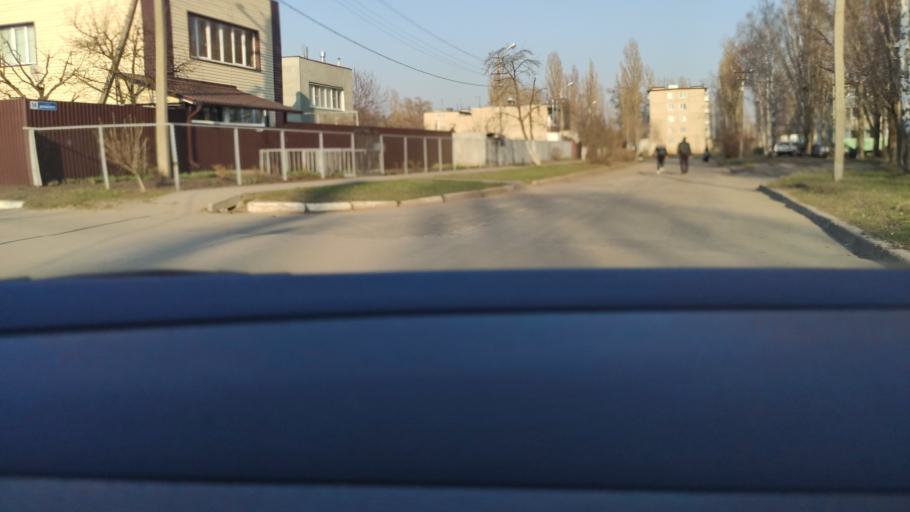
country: RU
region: Voronezj
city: Maslovka
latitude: 51.5864
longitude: 39.3169
